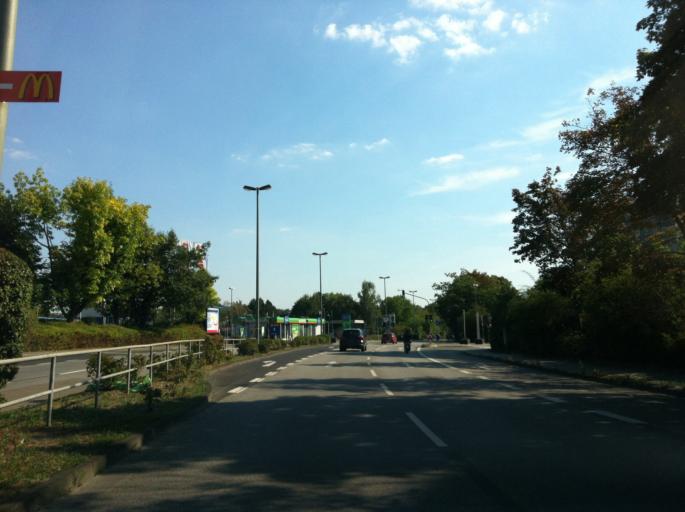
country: DE
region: Hesse
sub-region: Regierungsbezirk Darmstadt
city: Eschborn
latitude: 50.1365
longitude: 8.5986
